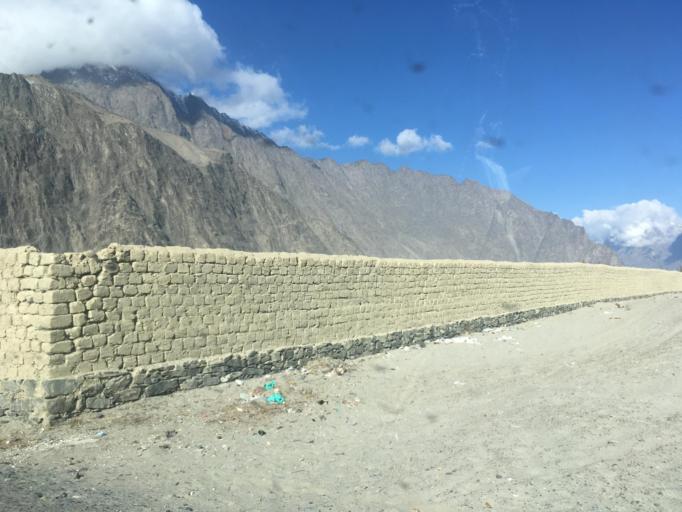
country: PK
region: Gilgit-Baltistan
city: Skardu
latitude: 35.3548
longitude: 75.5217
